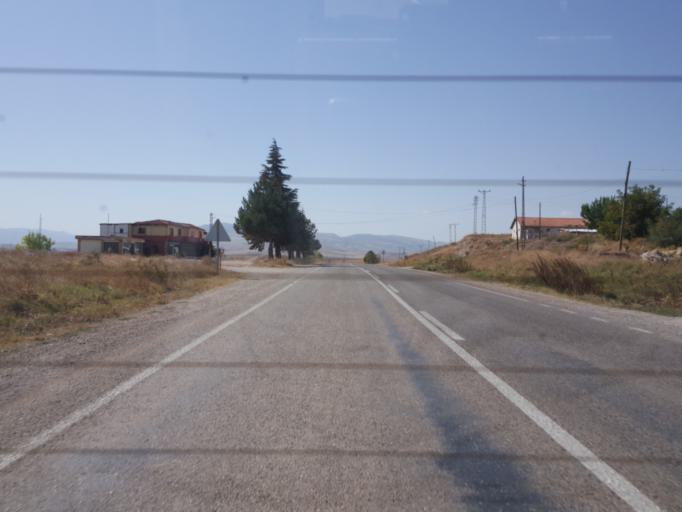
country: TR
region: Amasya
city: Dogantepe
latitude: 40.5802
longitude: 35.6364
